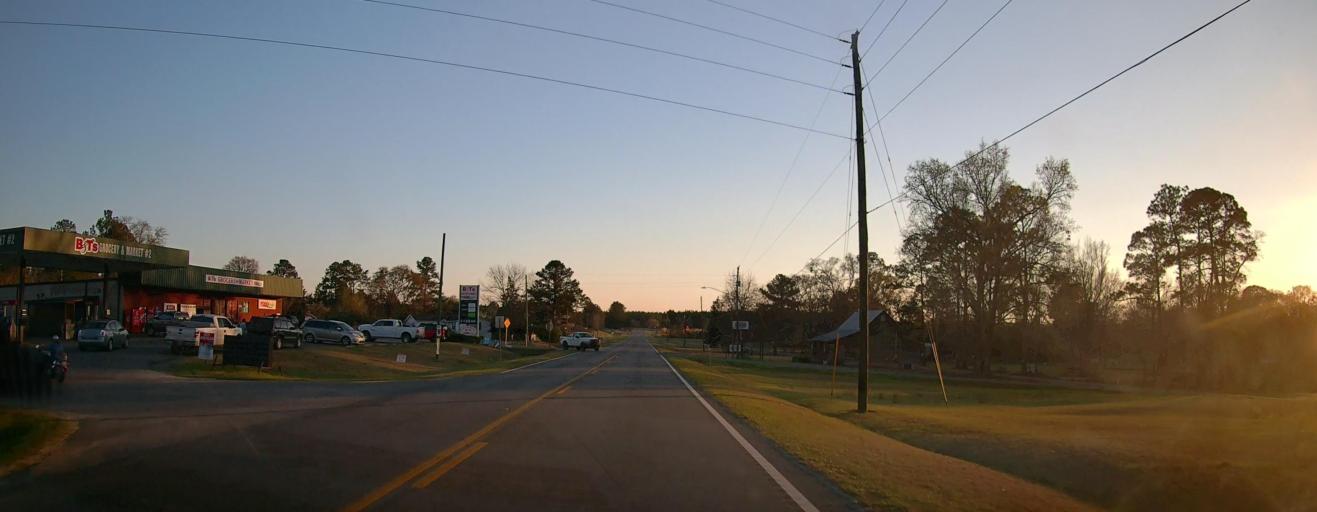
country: US
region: Georgia
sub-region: Dodge County
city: Chester
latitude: 32.3806
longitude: -82.9927
